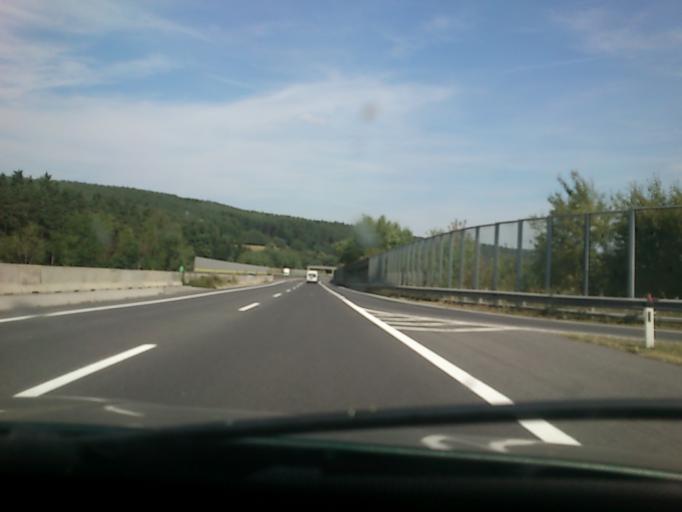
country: AT
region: Lower Austria
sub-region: Politischer Bezirk Neunkirchen
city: Seebenstein
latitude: 47.6740
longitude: 16.1256
